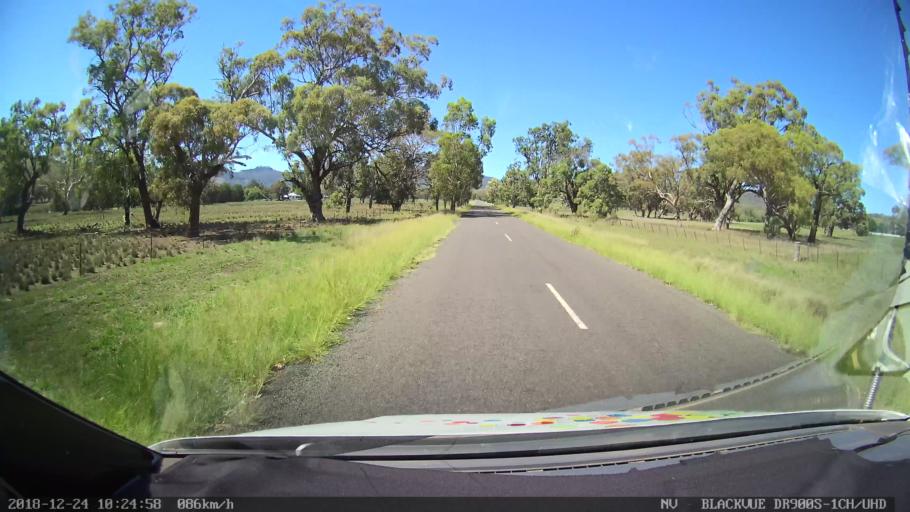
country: AU
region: New South Wales
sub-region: Liverpool Plains
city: Quirindi
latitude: -31.7930
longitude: 150.5305
